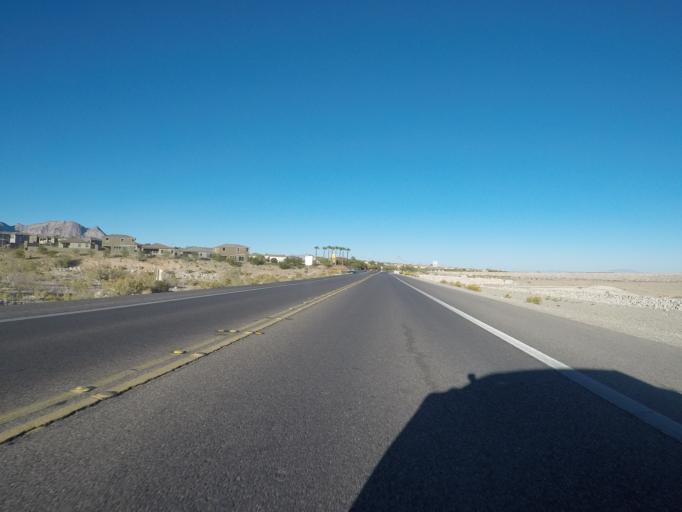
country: US
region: Nevada
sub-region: Clark County
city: Summerlin South
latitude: 36.1559
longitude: -115.3631
